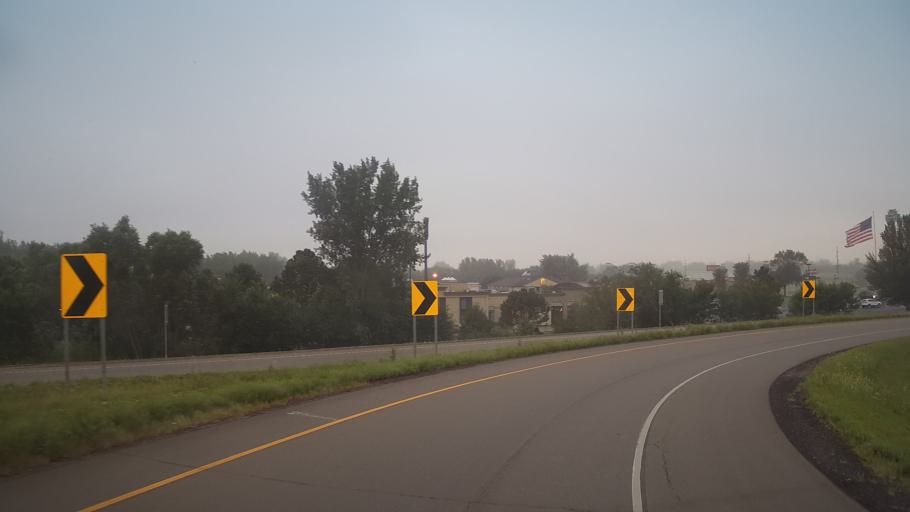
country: US
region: Minnesota
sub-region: Martin County
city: Fairmont
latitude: 43.6786
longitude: -94.4455
